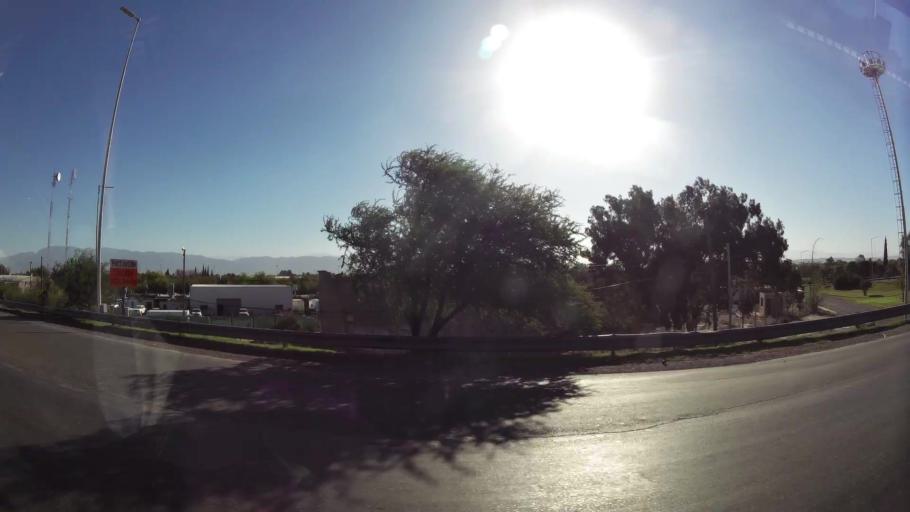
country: AR
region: San Juan
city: Villa Krause
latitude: -31.5563
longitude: -68.5138
